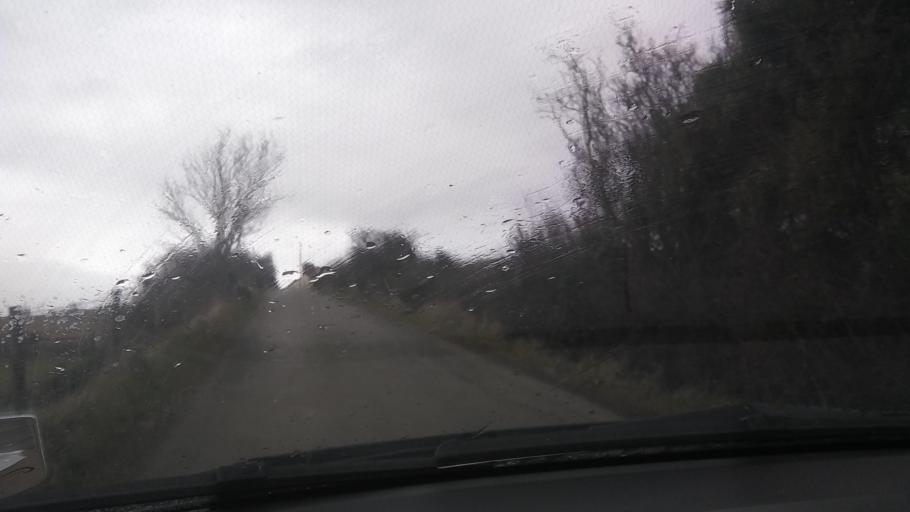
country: GB
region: England
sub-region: Worcestershire
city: Tenbury Wells
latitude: 52.3815
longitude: -2.6097
